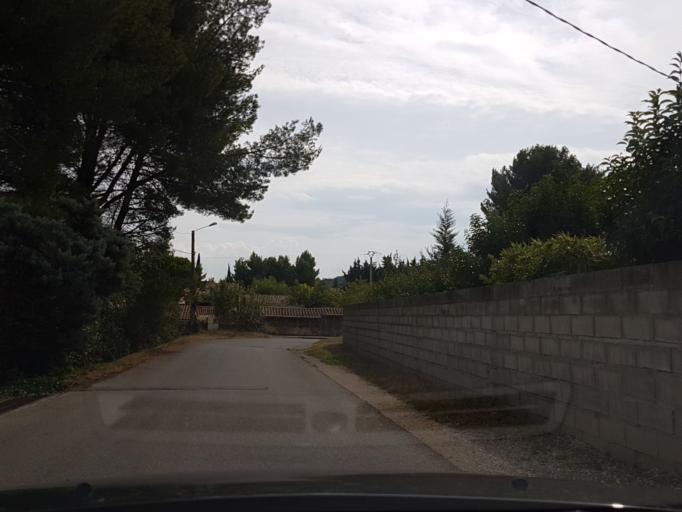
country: FR
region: Provence-Alpes-Cote d'Azur
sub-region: Departement du Vaucluse
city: Jonquerettes
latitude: 43.9520
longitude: 4.9334
